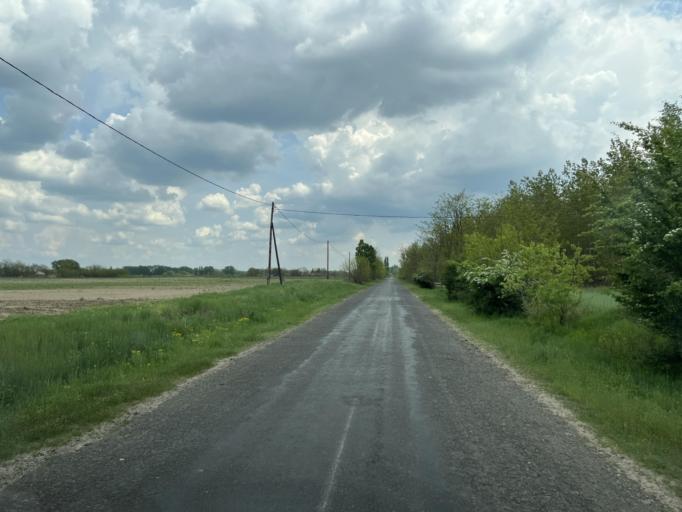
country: HU
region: Pest
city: Nagykoros
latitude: 47.0921
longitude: 19.7629
